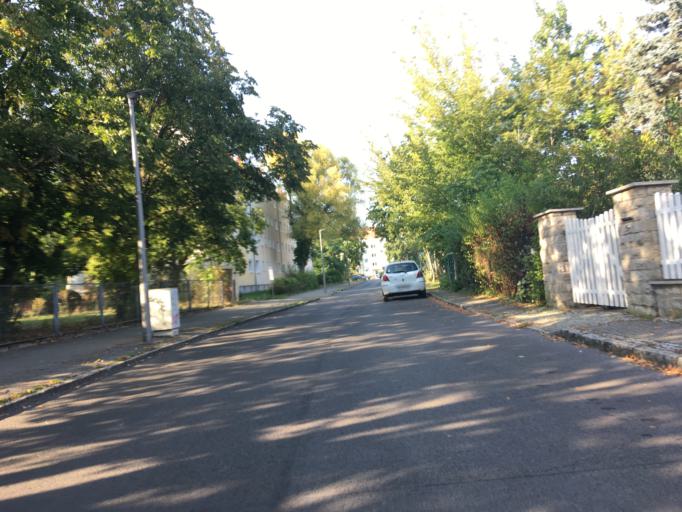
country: DE
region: Berlin
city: Grunau
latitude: 52.4237
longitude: 13.5937
